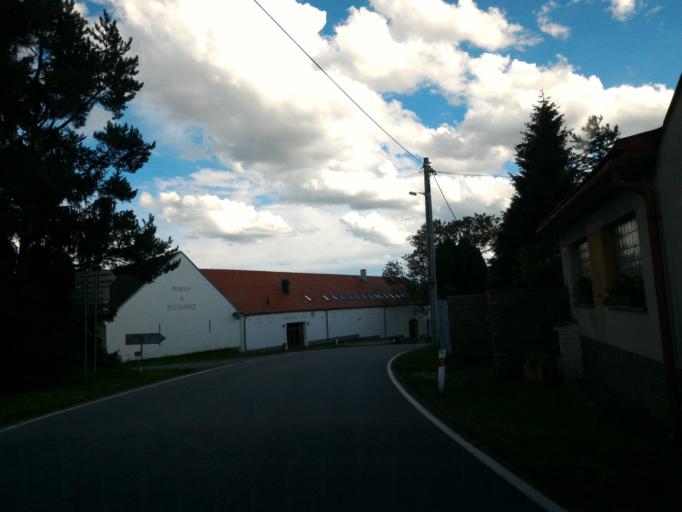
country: CZ
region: Vysocina
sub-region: Okres Jihlava
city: Telc
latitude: 49.2240
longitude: 15.4224
